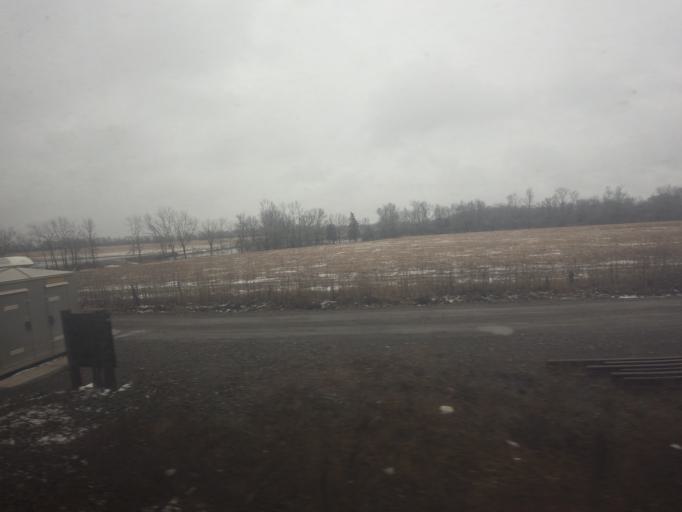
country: CA
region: Ontario
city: Deseronto
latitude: 44.2196
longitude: -77.1501
